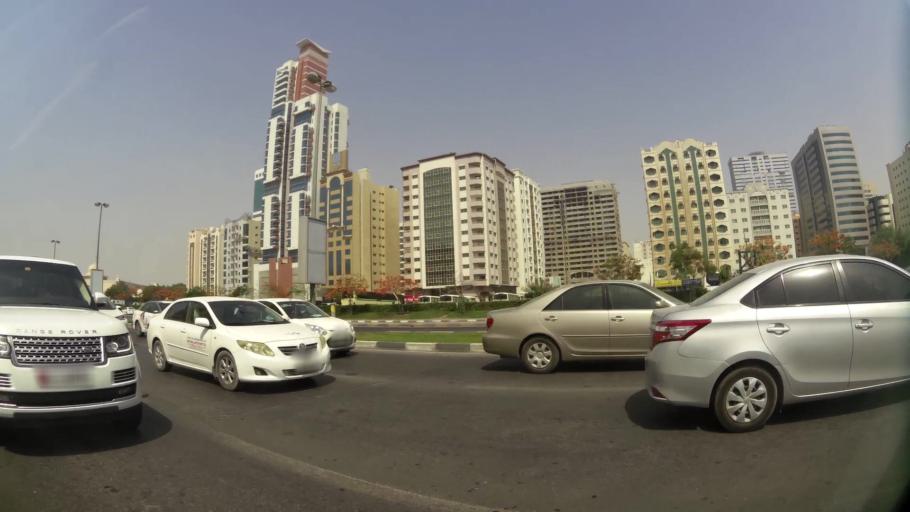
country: AE
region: Ash Shariqah
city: Sharjah
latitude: 25.3494
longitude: 55.3891
